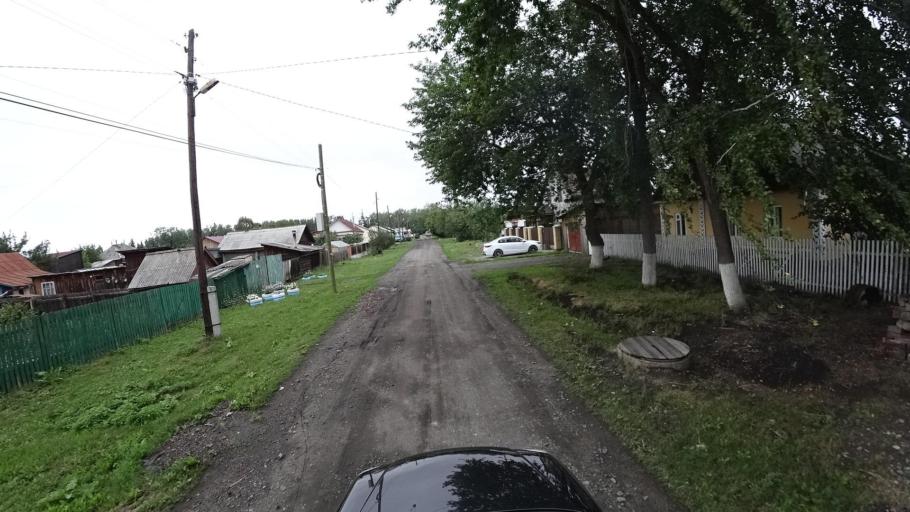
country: RU
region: Sverdlovsk
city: Kamyshlov
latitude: 56.8468
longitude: 62.7658
